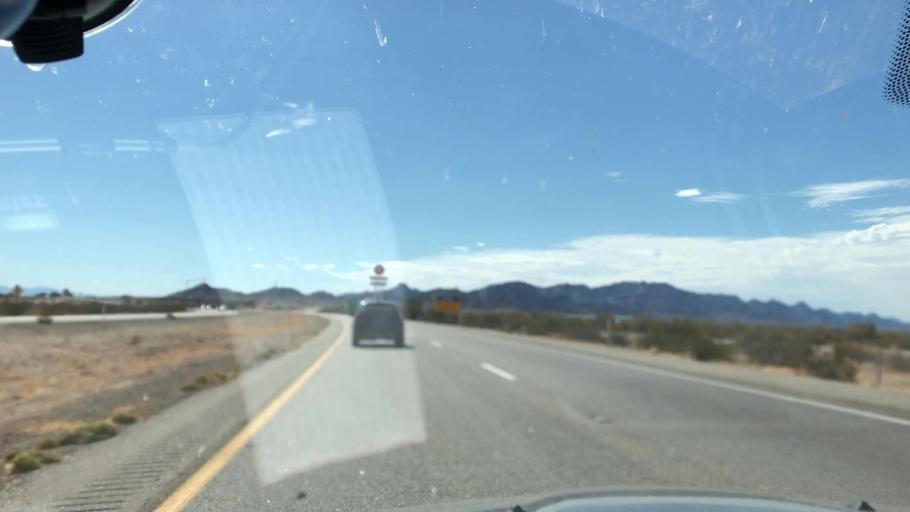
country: US
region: California
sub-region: Riverside County
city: Mesa Verde
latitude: 33.6087
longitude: -114.7195
